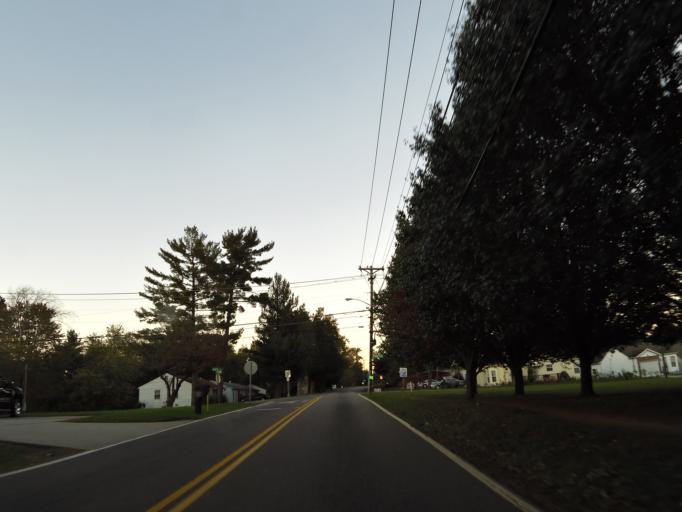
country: US
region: Tennessee
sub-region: Knox County
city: Knoxville
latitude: 36.0162
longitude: -83.9664
